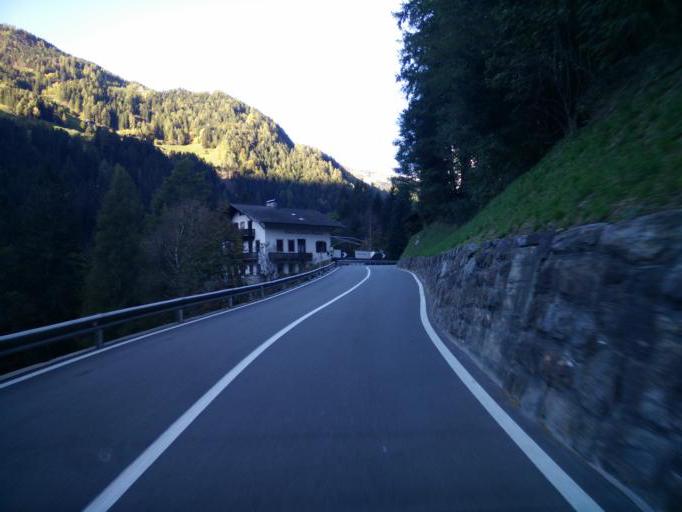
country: IT
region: Trentino-Alto Adige
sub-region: Bolzano
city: San Leonardo in Passiria
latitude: 46.8177
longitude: 11.2355
